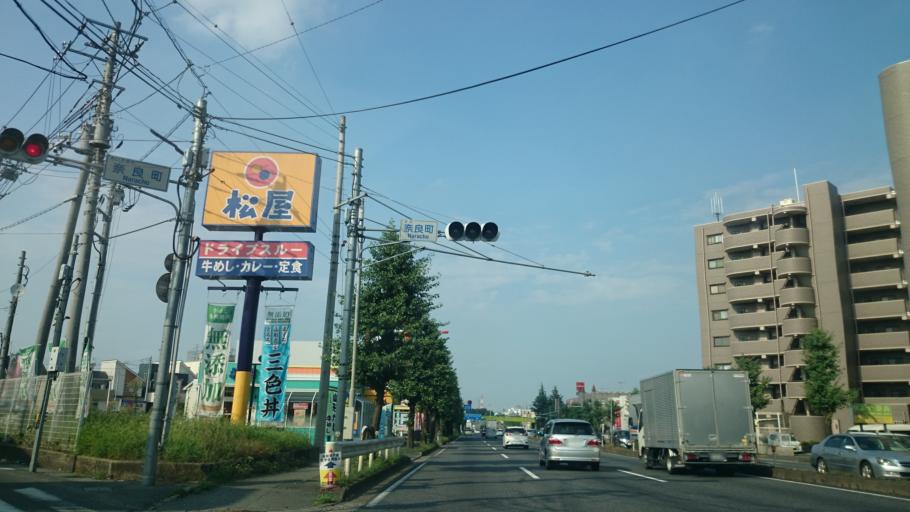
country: JP
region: Saitama
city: Ageoshimo
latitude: 35.9408
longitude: 139.6028
